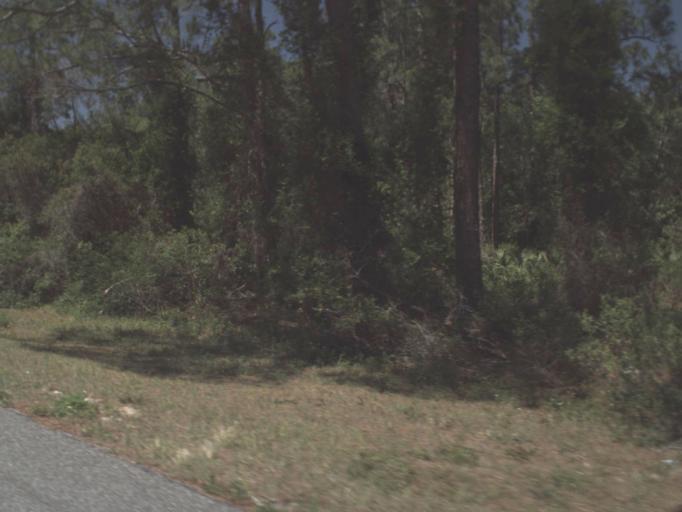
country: US
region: Florida
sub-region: Lake County
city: Astor
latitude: 29.1291
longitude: -81.6222
